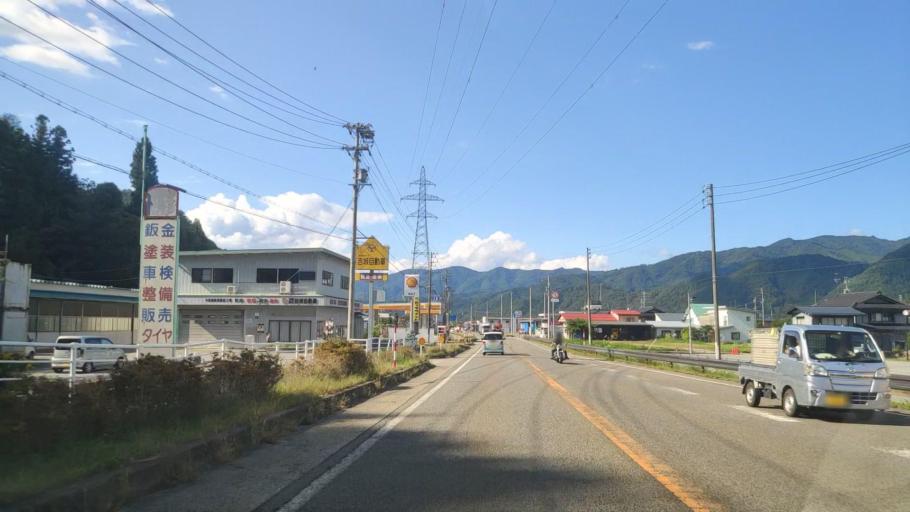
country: JP
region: Gifu
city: Takayama
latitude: 36.2312
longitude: 137.1805
